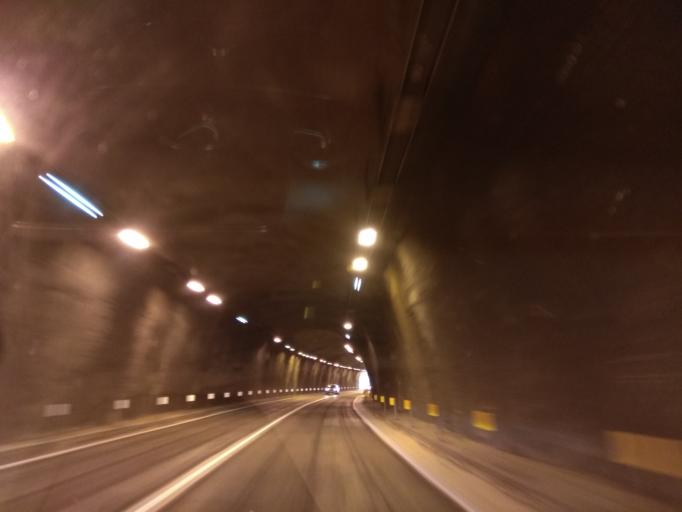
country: ES
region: Catalonia
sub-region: Provincia de Lleida
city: Tiurana
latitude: 41.9875
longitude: 1.2935
